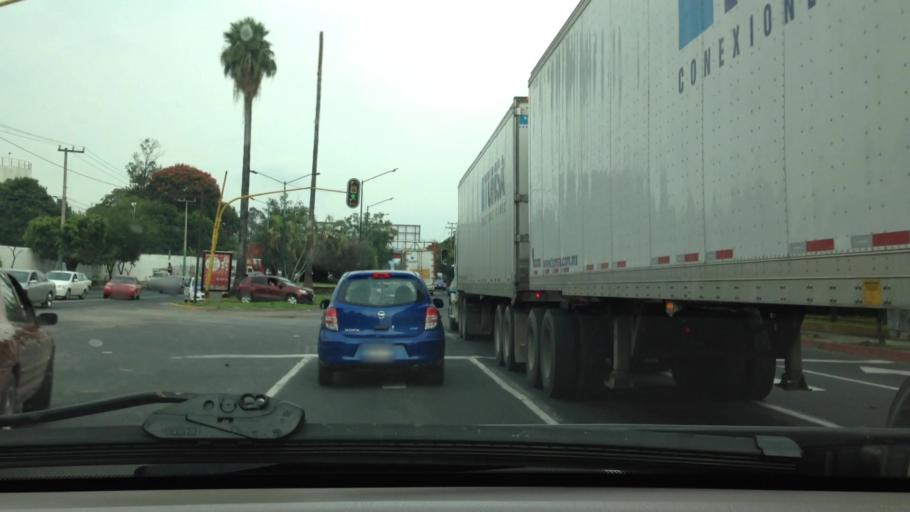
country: MX
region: Morelos
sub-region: Tepoztlan
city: Loma Bonita
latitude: 18.9196
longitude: -99.1928
